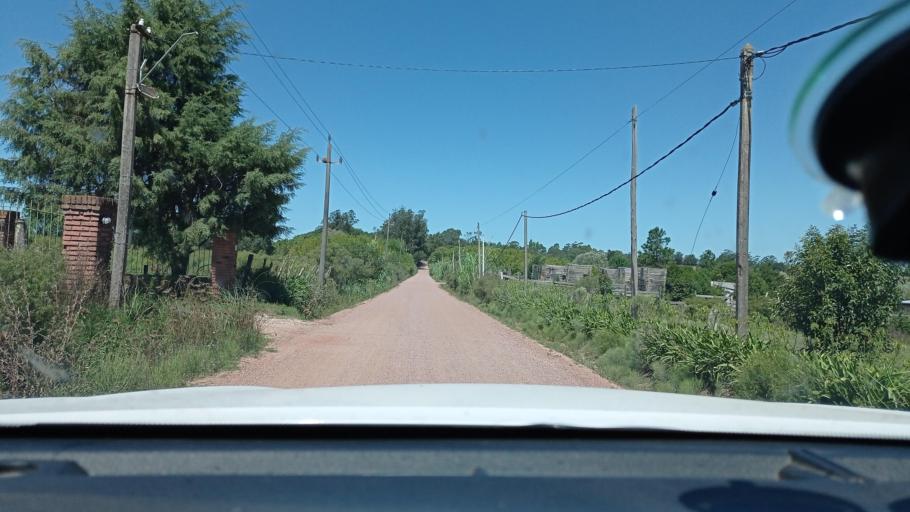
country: UY
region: Canelones
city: La Paz
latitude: -34.7503
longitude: -56.1971
